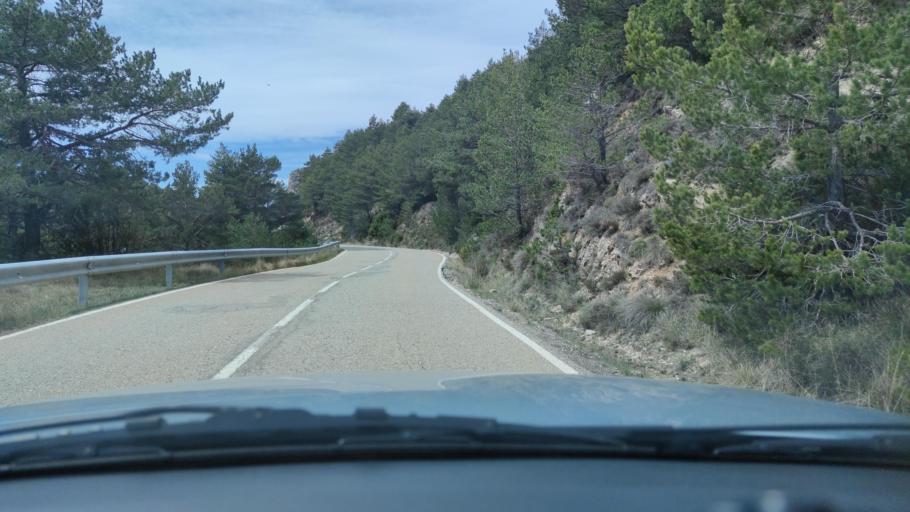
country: ES
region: Catalonia
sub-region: Provincia de Lleida
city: Olius
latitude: 42.1407
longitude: 1.5430
